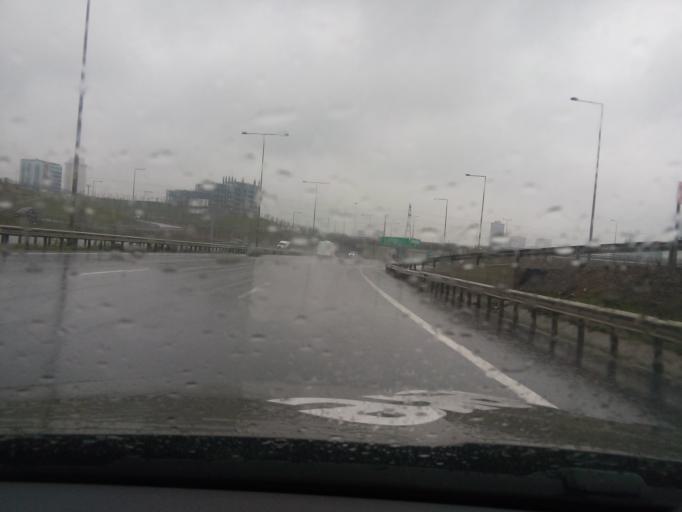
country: TR
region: Istanbul
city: Basaksehir
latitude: 41.0746
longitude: 28.8154
